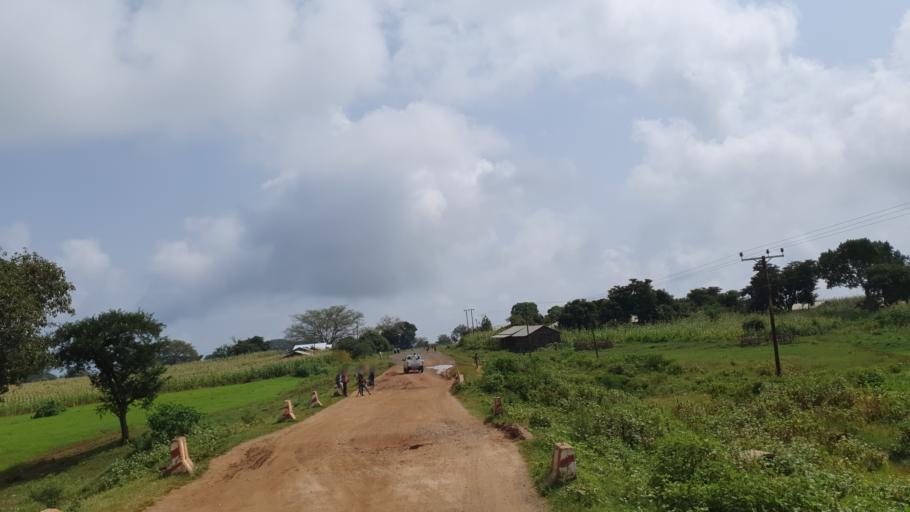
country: ET
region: Amhara
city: Bure
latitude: 10.1907
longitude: 36.9658
